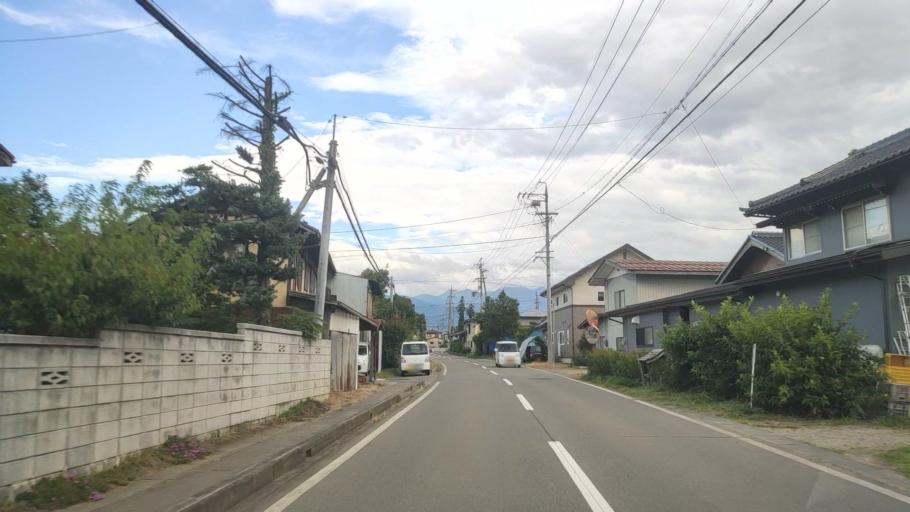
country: JP
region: Nagano
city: Nakano
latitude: 36.7776
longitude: 138.3557
